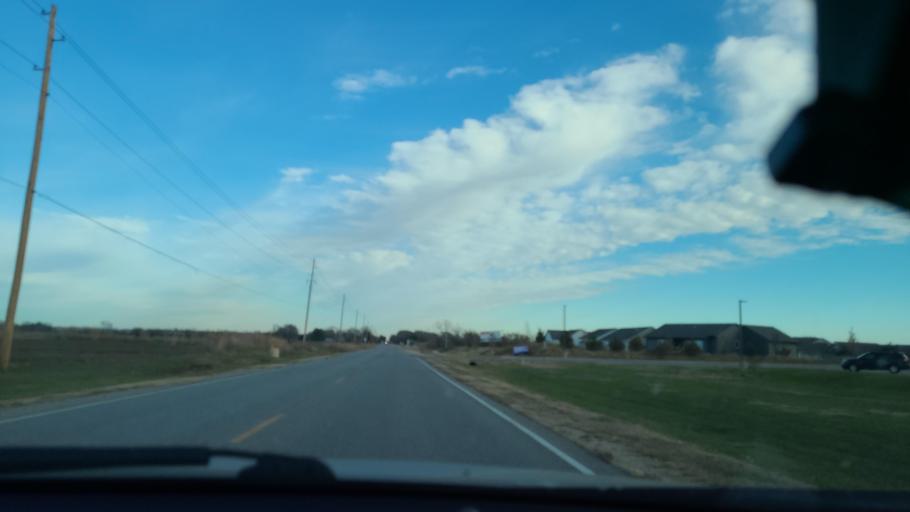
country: US
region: Kansas
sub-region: Sedgwick County
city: Goddard
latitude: 37.6496
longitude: -97.5630
